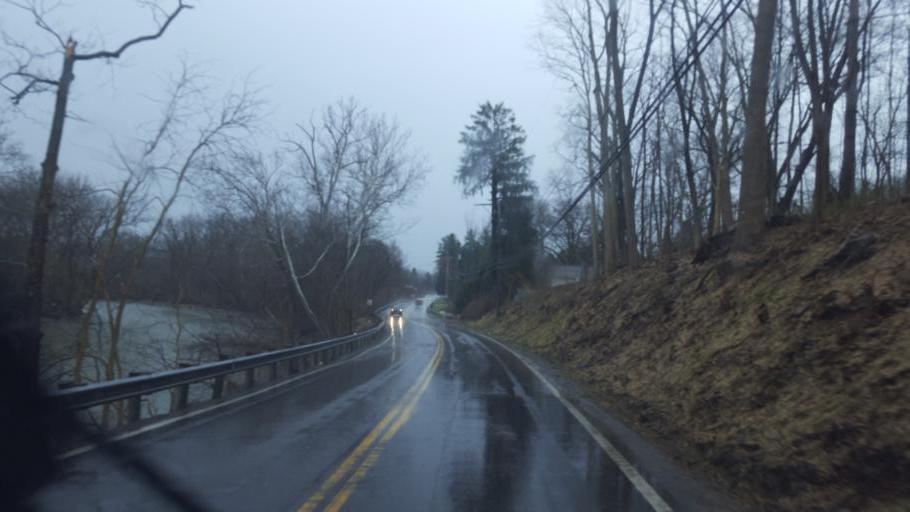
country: US
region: Ohio
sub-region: Delaware County
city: Powell
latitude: 40.1504
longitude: -83.0443
